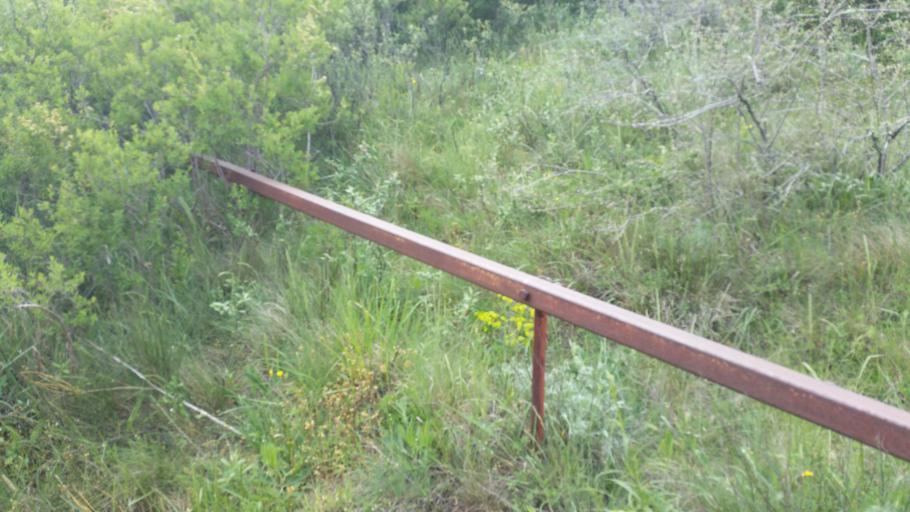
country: AZ
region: Agstafa
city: Saloglu
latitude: 41.4467
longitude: 45.3738
